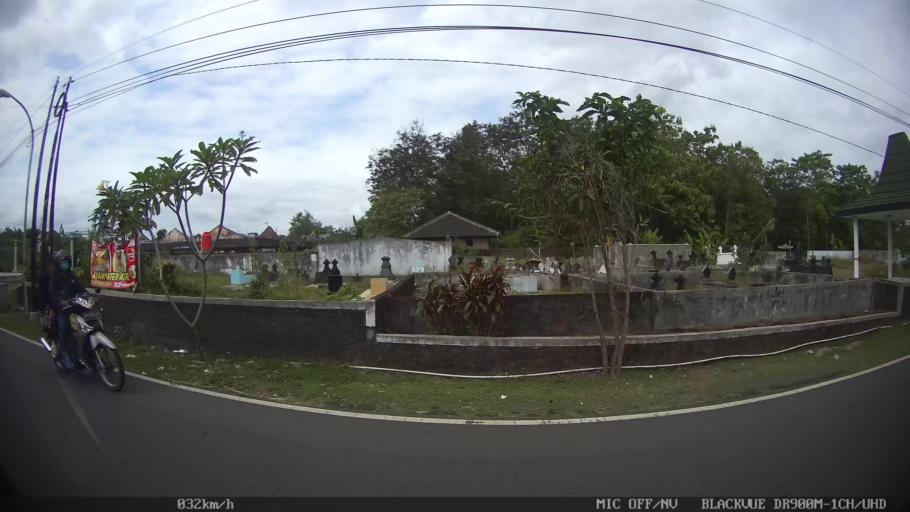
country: ID
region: Daerah Istimewa Yogyakarta
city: Depok
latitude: -7.8064
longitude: 110.4611
